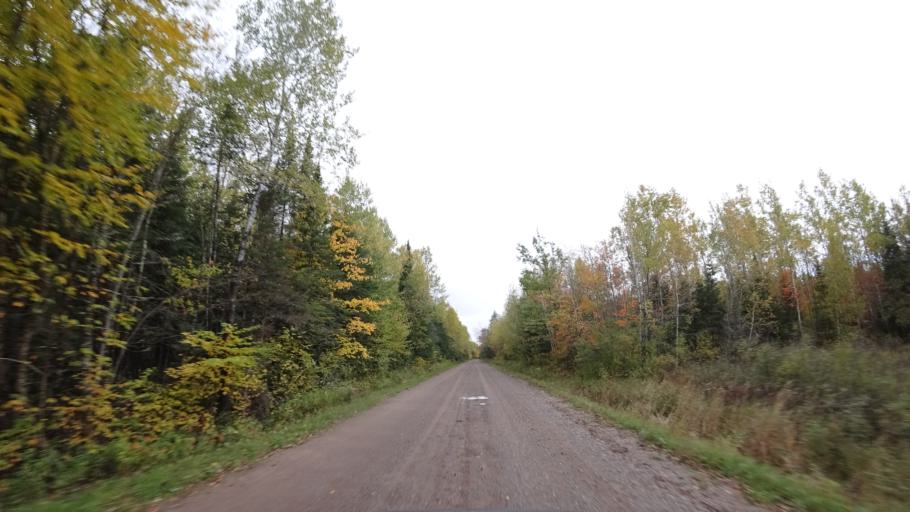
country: US
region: Wisconsin
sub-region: Sawyer County
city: Little Round Lake
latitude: 45.9725
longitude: -90.9844
